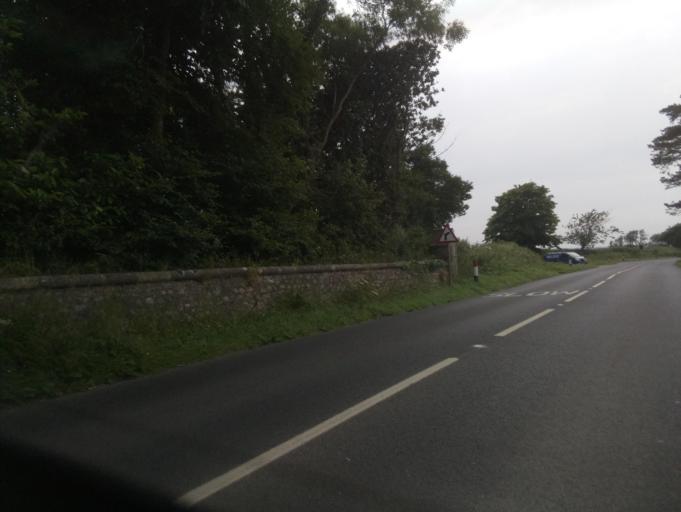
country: GB
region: England
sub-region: Devon
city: Axminster
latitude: 50.7167
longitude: -3.0015
